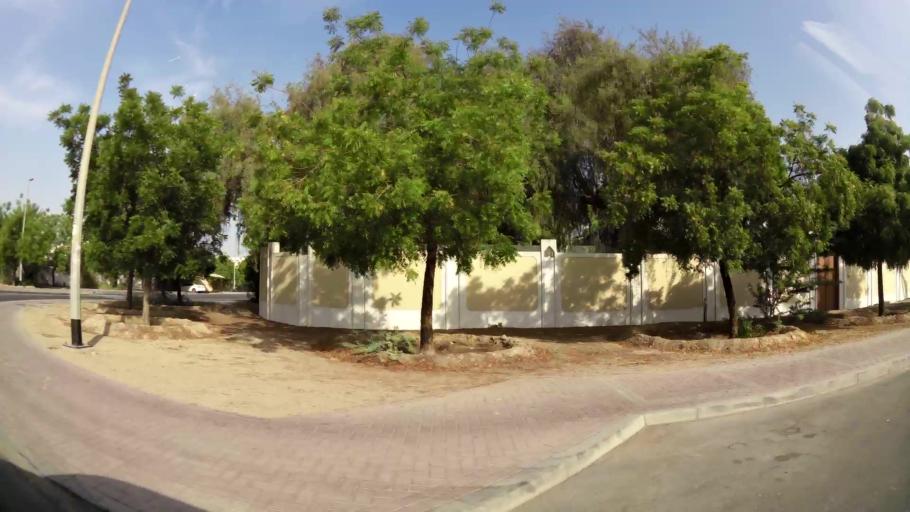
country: AE
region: Ash Shariqah
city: Sharjah
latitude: 25.2295
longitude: 55.3821
